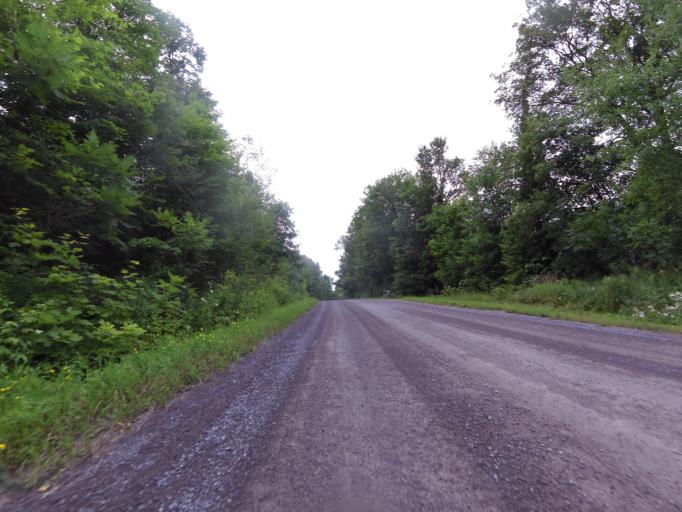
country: CA
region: Ontario
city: Carleton Place
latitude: 45.1652
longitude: -76.2741
